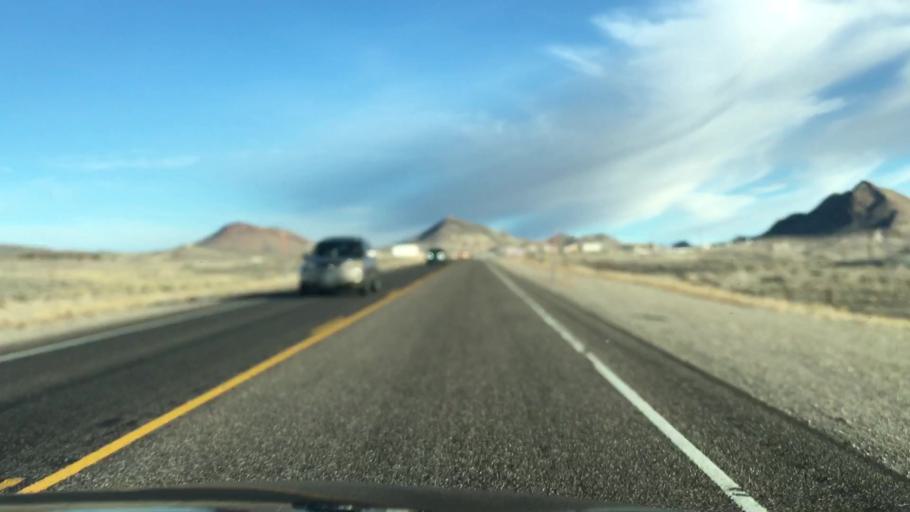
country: US
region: Nevada
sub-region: Nye County
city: Tonopah
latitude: 38.0809
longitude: -117.2650
